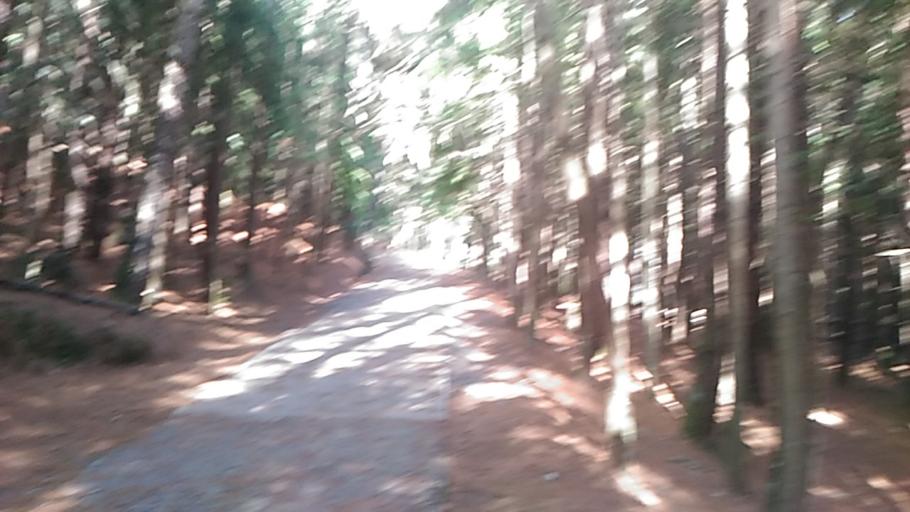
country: TW
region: Taiwan
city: Daxi
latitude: 24.4046
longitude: 121.3075
